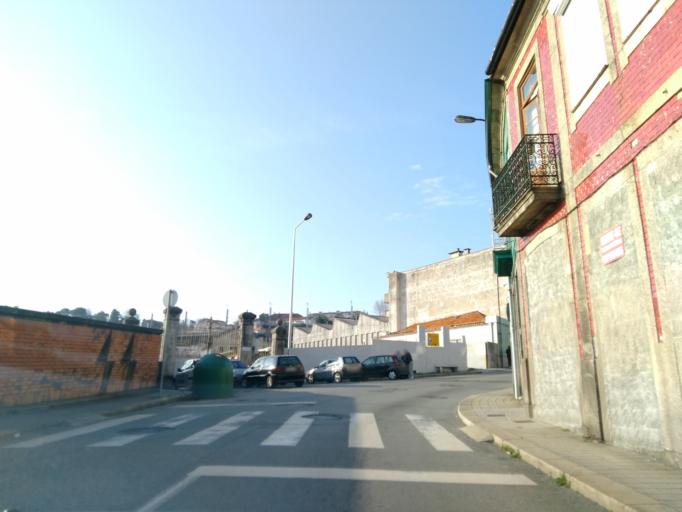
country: PT
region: Porto
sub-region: Vila Nova de Gaia
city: Oliveira do Douro
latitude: 41.1449
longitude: -8.5827
